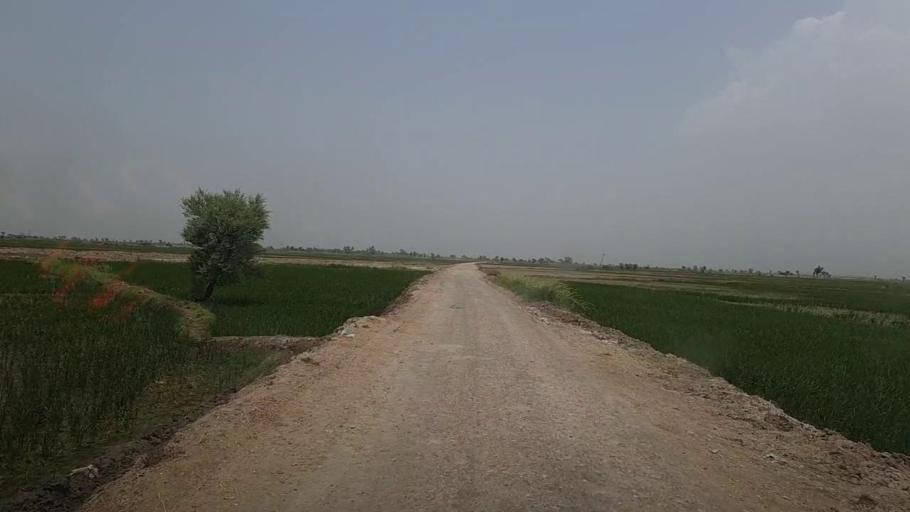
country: PK
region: Sindh
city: Sita Road
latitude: 27.0704
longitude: 67.8650
